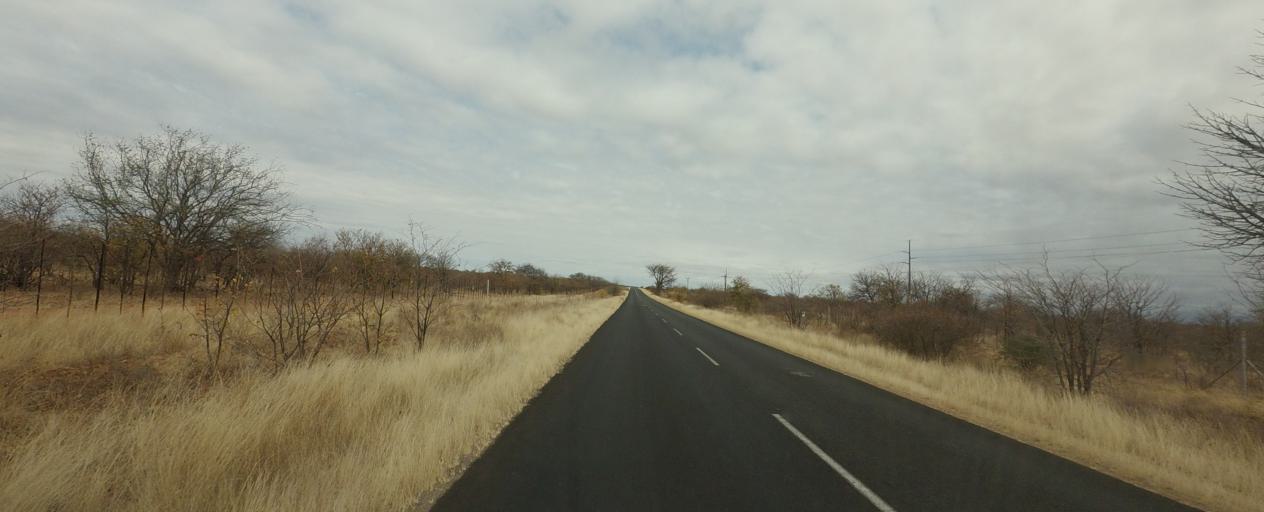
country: ZW
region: Matabeleland South
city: Beitbridge
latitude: -22.4310
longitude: 29.4552
